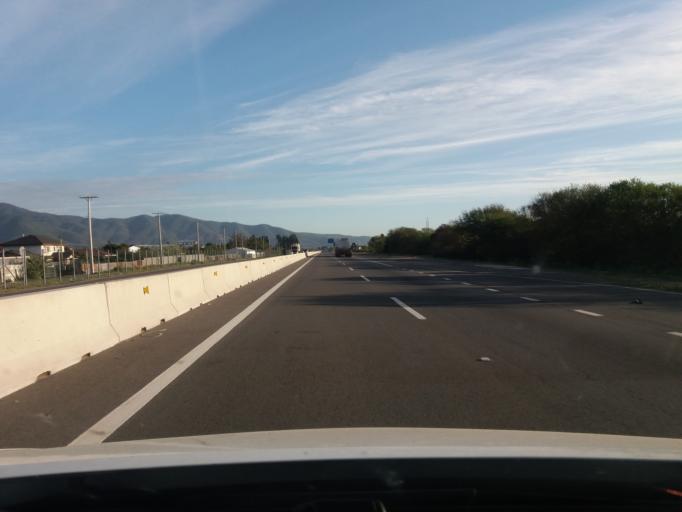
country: CL
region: Valparaiso
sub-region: Provincia de Quillota
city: Quillota
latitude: -32.8640
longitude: -71.2271
